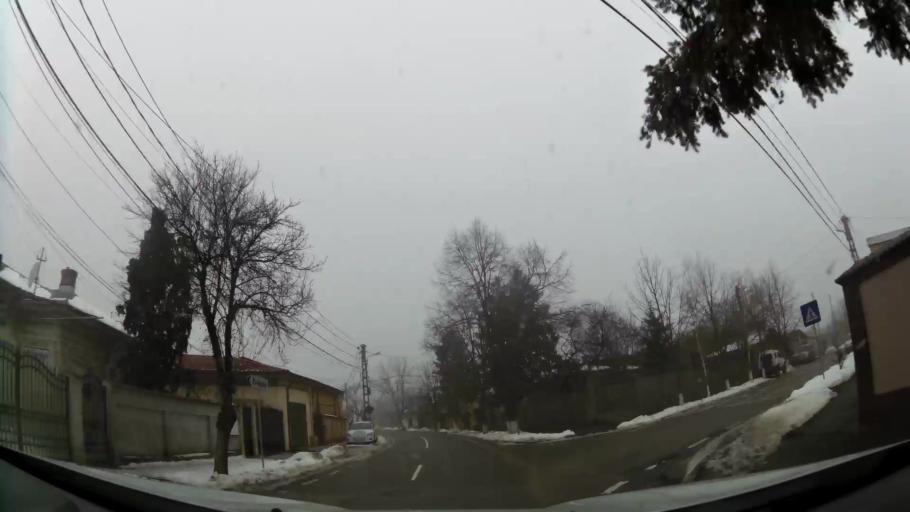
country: RO
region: Ilfov
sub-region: Comuna Chiajna
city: Chiajna
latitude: 44.4591
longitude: 25.9801
